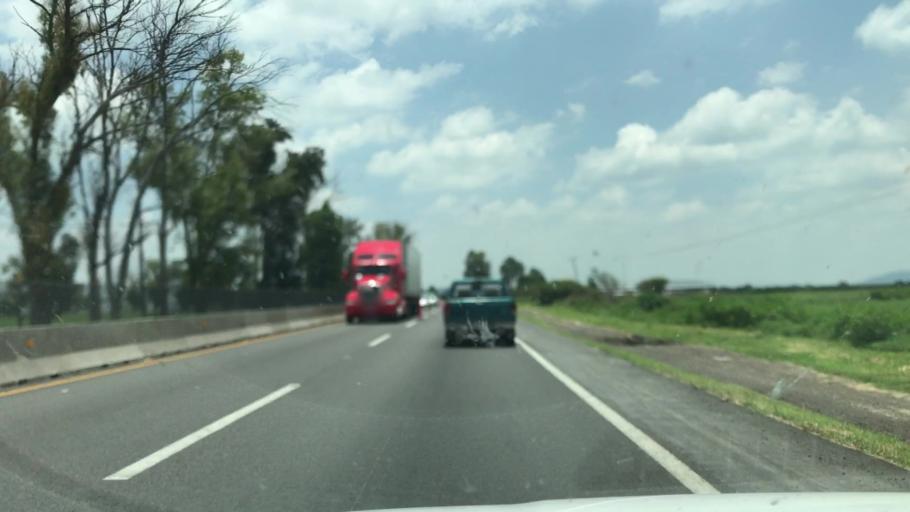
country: MX
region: Guanajuato
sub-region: Abasolo
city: San Bernardo Pena Blanca
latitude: 20.5049
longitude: -101.4756
